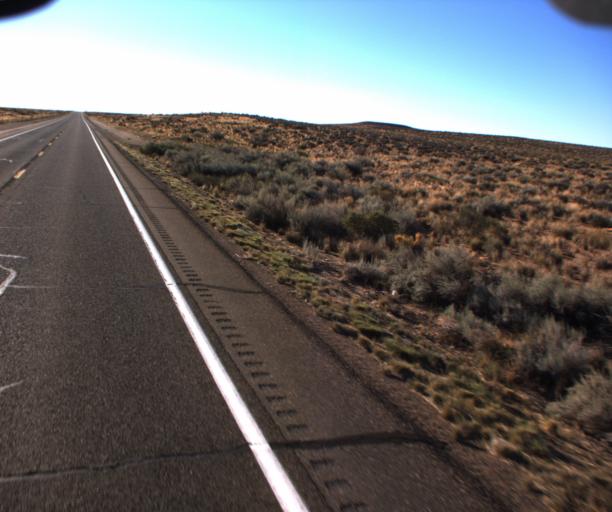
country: US
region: Arizona
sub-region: Coconino County
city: Page
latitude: 36.9737
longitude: -111.5171
